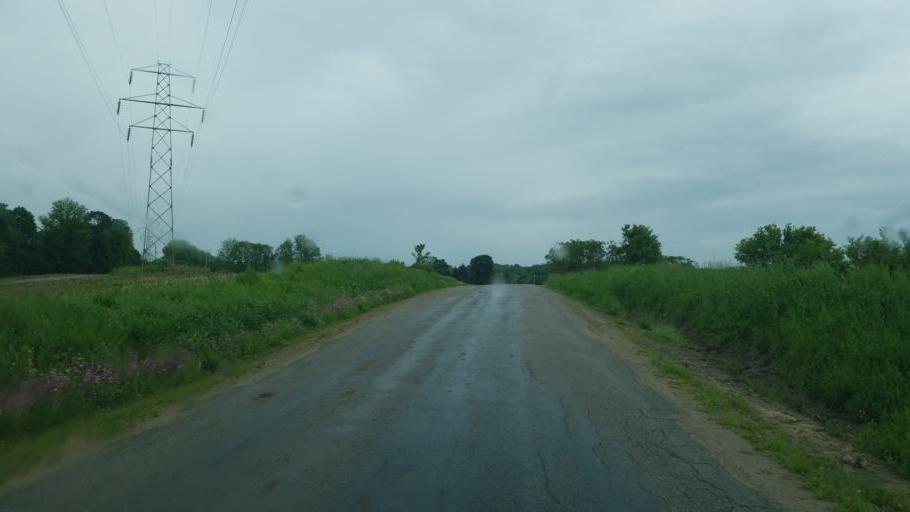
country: US
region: New York
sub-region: Herkimer County
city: Frankfort
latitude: 43.0699
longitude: -75.0591
